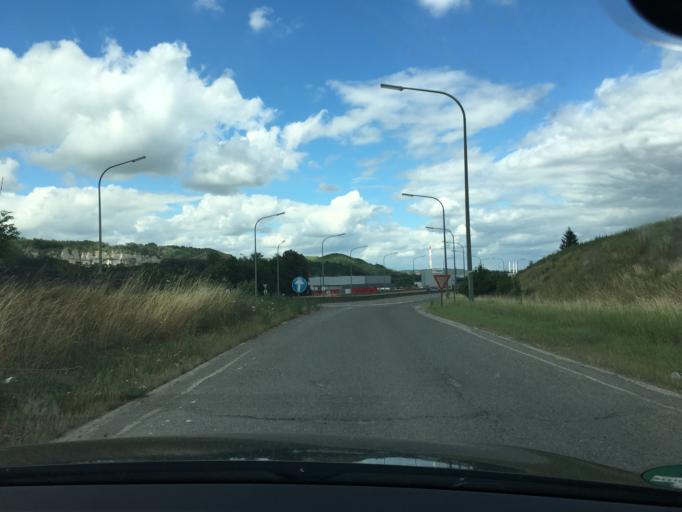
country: BE
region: Wallonia
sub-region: Province de Liege
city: Engis
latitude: 50.5608
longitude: 5.3623
